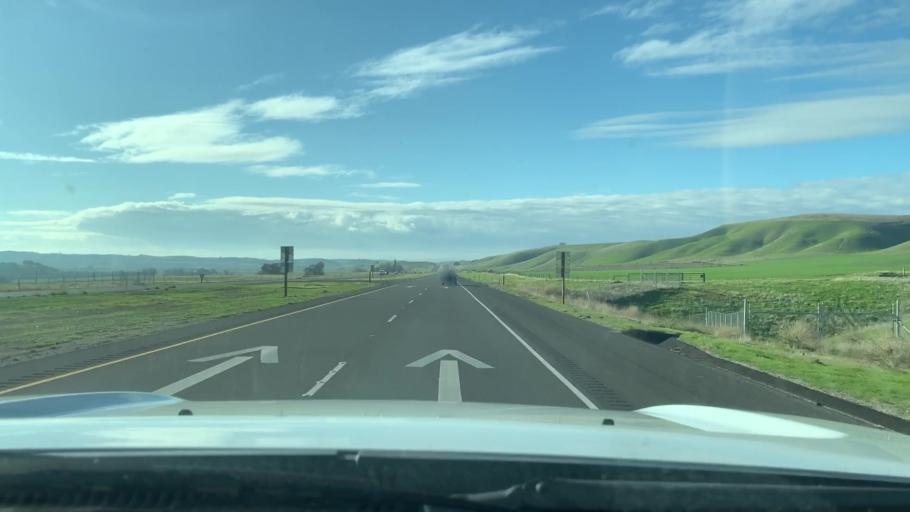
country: US
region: California
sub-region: San Luis Obispo County
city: Shandon
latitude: 35.6608
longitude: -120.4502
